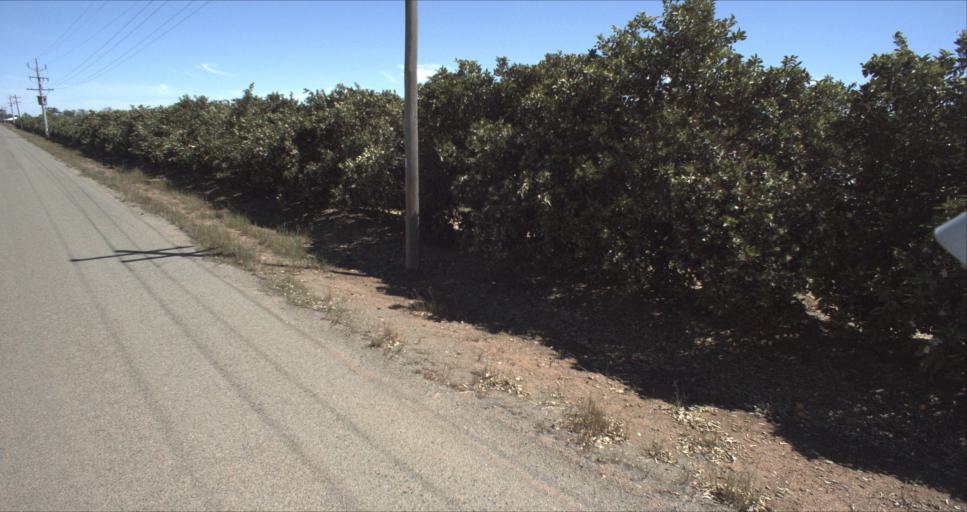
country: AU
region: New South Wales
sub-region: Leeton
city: Leeton
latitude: -34.5341
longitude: 146.3527
